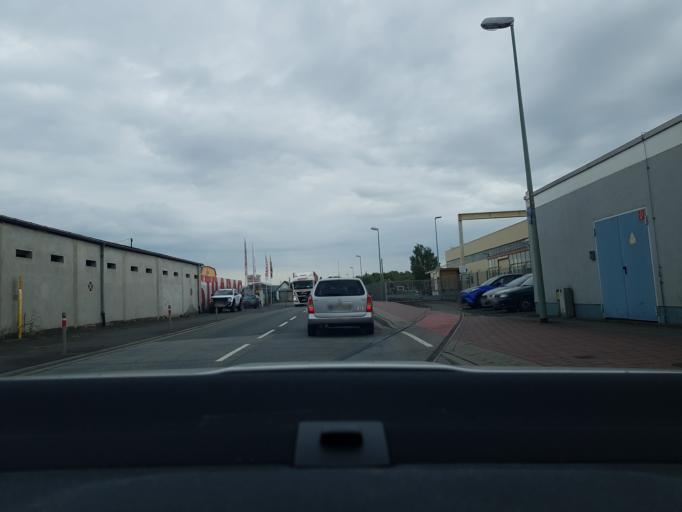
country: DE
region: Hesse
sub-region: Regierungsbezirk Giessen
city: Limburg an der Lahn
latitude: 50.3771
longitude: 8.0544
